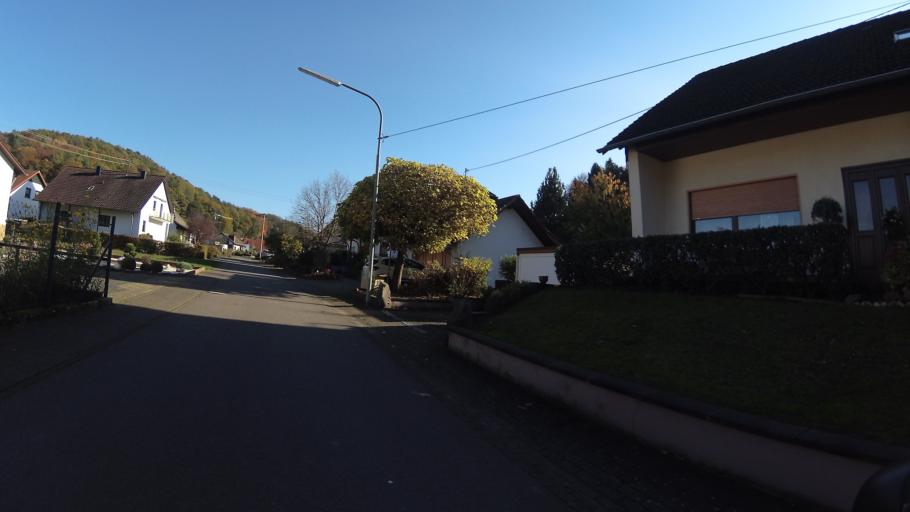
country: DE
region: Saarland
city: Losheim
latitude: 49.4733
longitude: 6.7210
